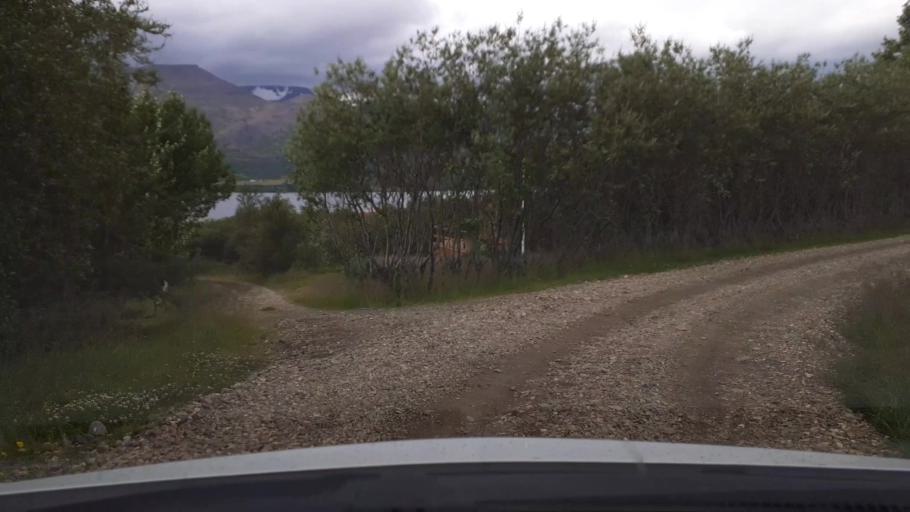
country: IS
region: West
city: Borgarnes
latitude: 64.5407
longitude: -21.5454
